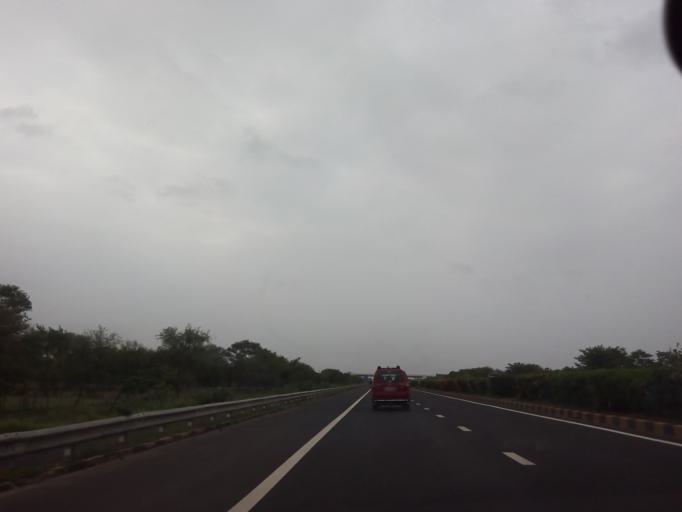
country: IN
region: Gujarat
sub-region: Kheda
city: Mahemdavad
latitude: 22.8119
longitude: 72.8341
